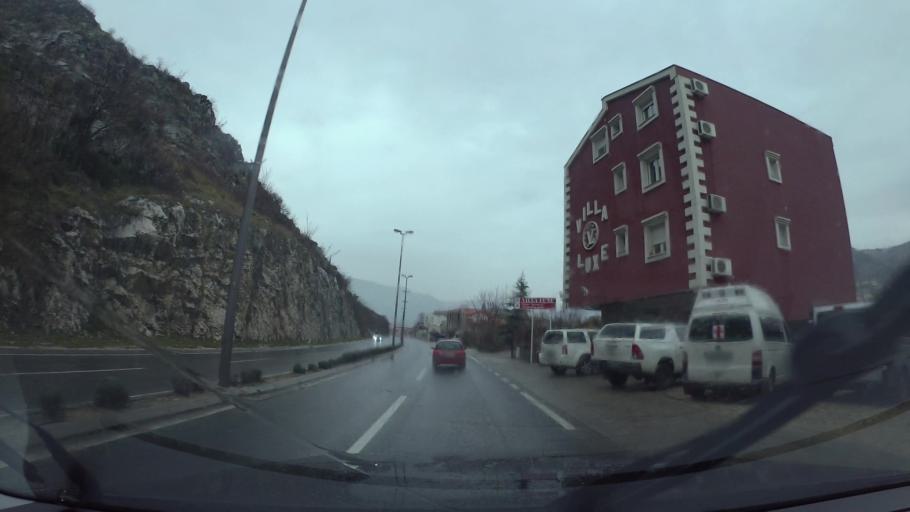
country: BA
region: Federation of Bosnia and Herzegovina
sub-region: Hercegovacko-Bosanski Kanton
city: Mostar
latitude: 43.3315
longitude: 17.8152
